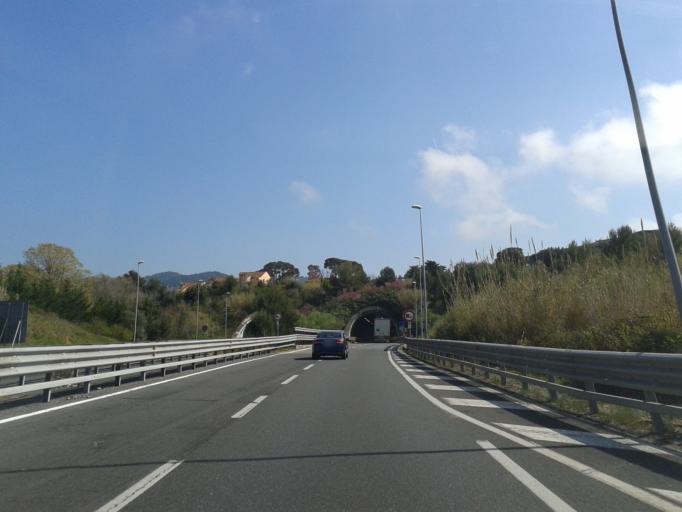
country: IT
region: Tuscany
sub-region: Provincia di Livorno
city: Livorno
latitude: 43.5105
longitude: 10.3346
